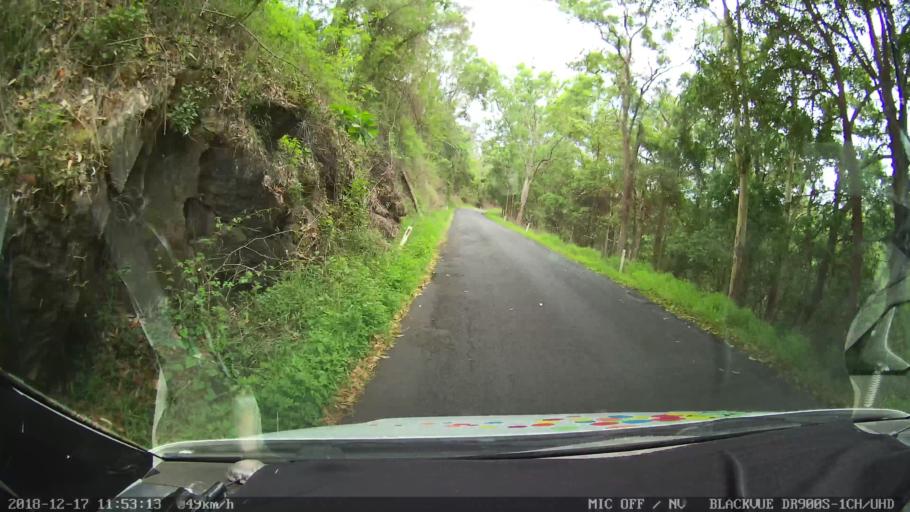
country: AU
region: New South Wales
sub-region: Kyogle
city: Kyogle
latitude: -28.5758
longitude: 152.5871
